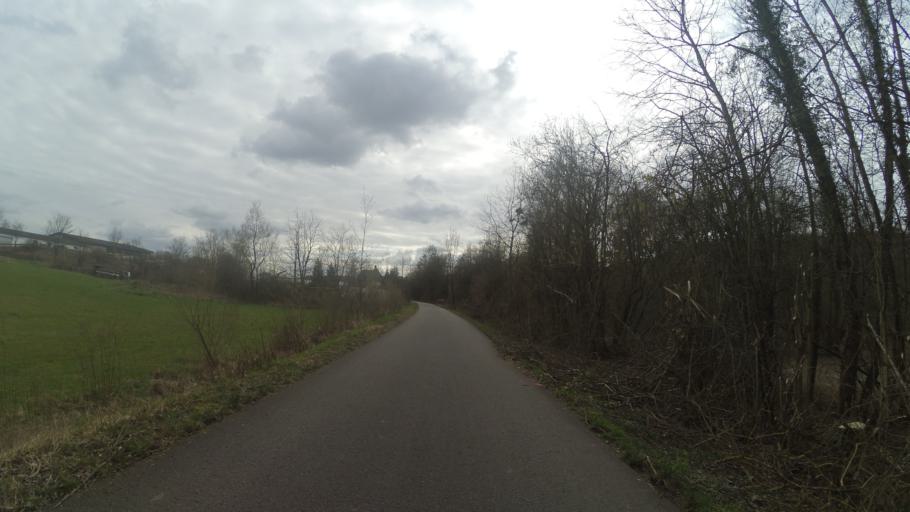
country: DE
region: Saarland
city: Gersheim
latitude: 49.1568
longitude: 7.2083
